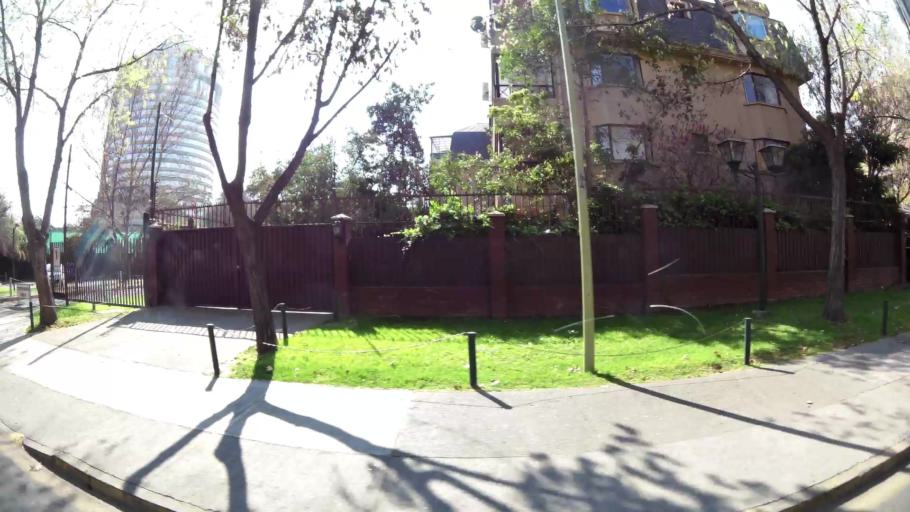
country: CL
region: Santiago Metropolitan
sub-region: Provincia de Santiago
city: Villa Presidente Frei, Nunoa, Santiago, Chile
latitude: -33.4047
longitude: -70.5815
